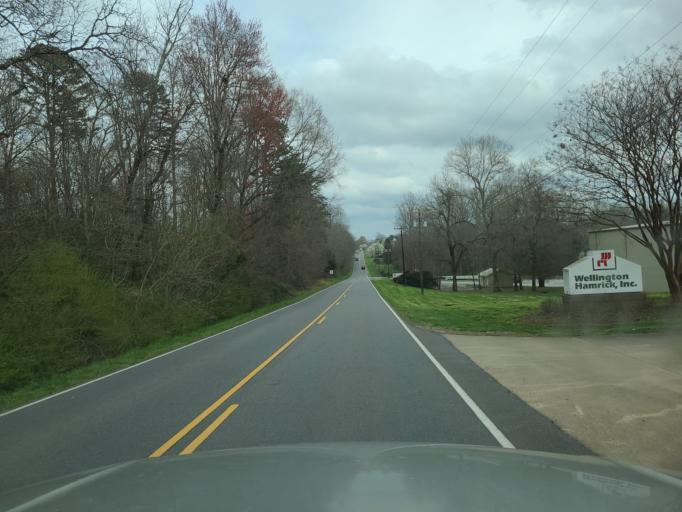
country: US
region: North Carolina
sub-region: Cleveland County
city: Boiling Springs
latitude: 35.2542
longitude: -81.6836
